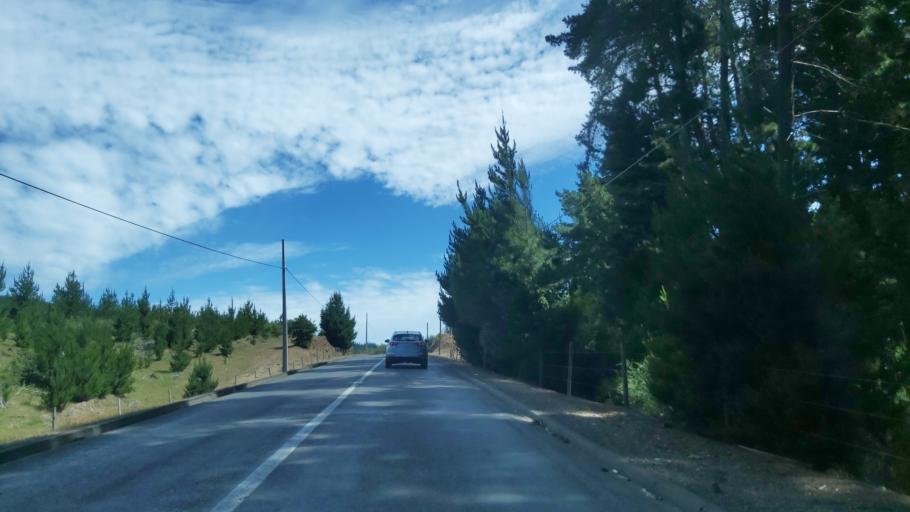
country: CL
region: Maule
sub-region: Provincia de Talca
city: Constitucion
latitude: -35.5157
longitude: -72.5296
